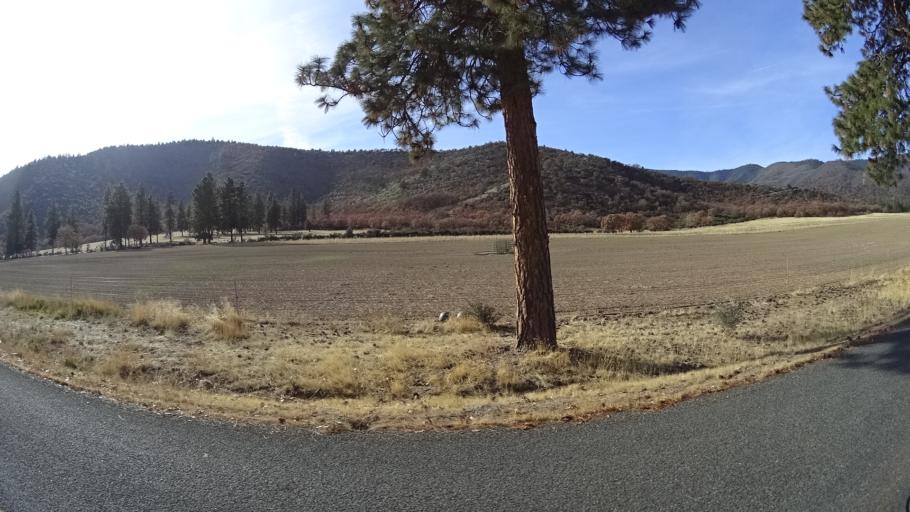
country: US
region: California
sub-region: Siskiyou County
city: Montague
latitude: 41.5395
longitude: -122.5857
